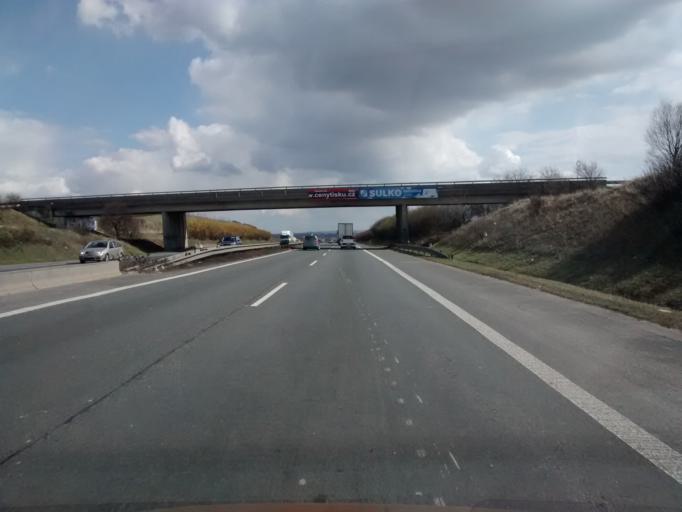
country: CZ
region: Central Bohemia
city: Zdiby
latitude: 50.1659
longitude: 14.4677
